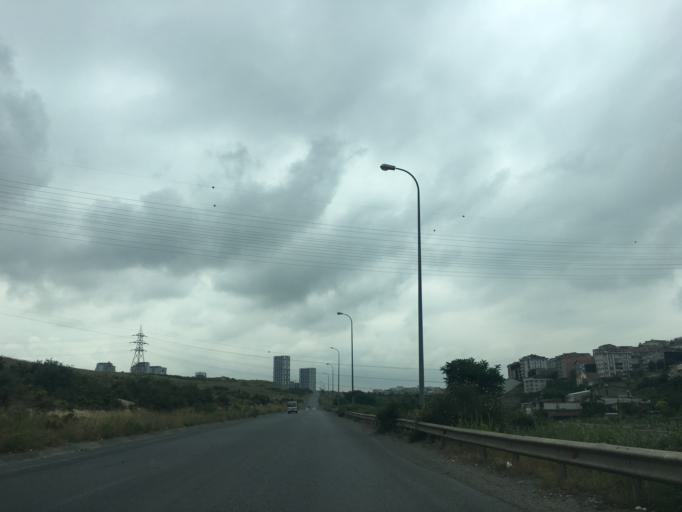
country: TR
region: Istanbul
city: Basaksehir
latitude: 41.0702
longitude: 28.7594
